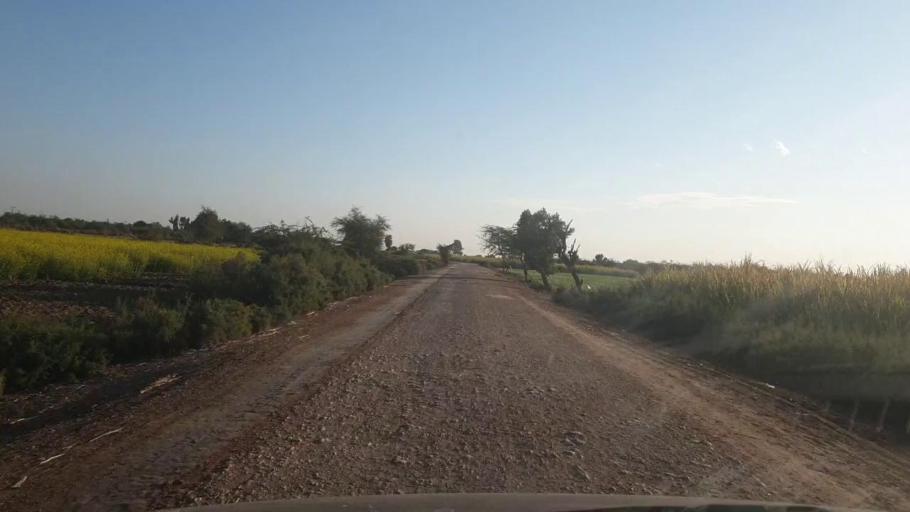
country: PK
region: Sindh
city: Sinjhoro
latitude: 26.0368
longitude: 68.8712
